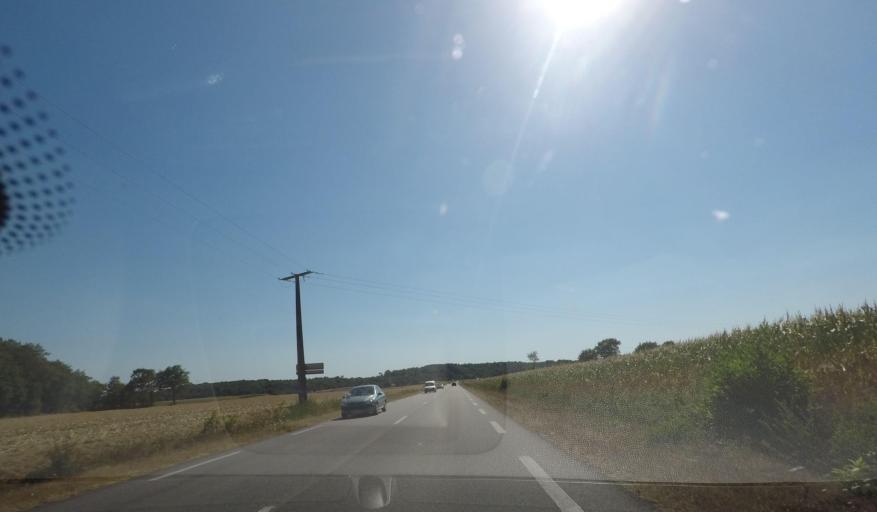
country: FR
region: Brittany
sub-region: Departement du Morbihan
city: Peaule
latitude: 47.5706
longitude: -2.3858
